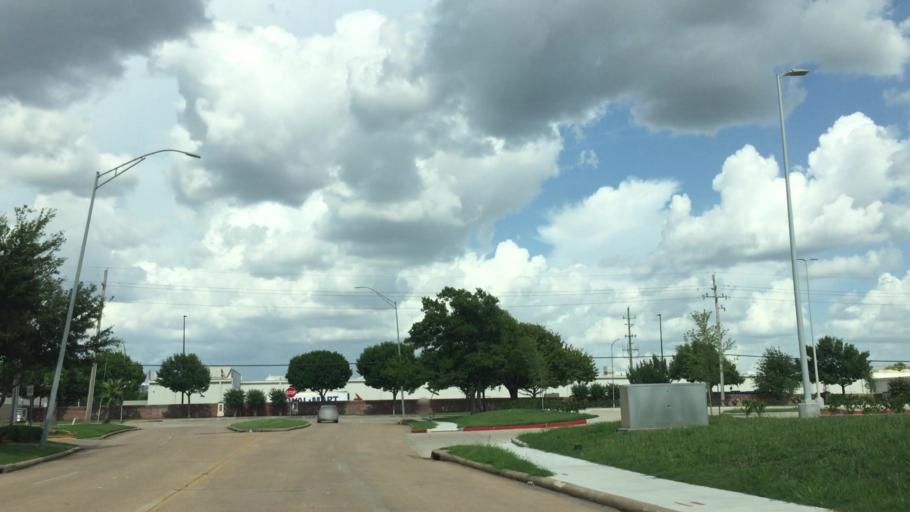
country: US
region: Texas
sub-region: Harris County
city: Bunker Hill Village
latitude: 29.7338
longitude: -95.5936
